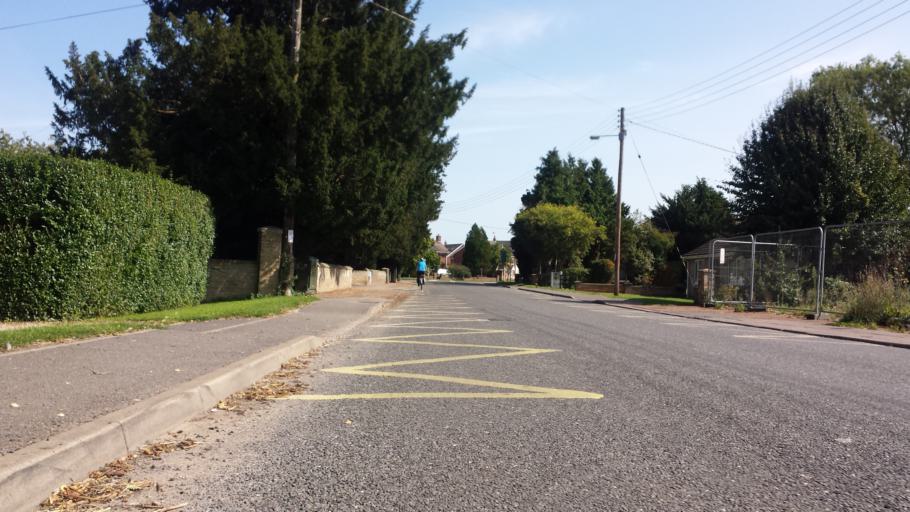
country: GB
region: England
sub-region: Cambridgeshire
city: Isleham
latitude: 52.3571
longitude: 0.4553
